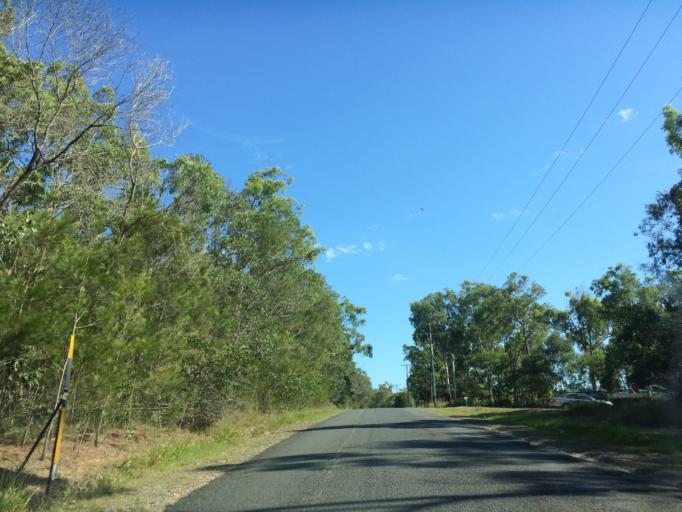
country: AU
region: Queensland
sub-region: Ipswich
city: Springfield Lakes
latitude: -27.7067
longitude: 152.9568
